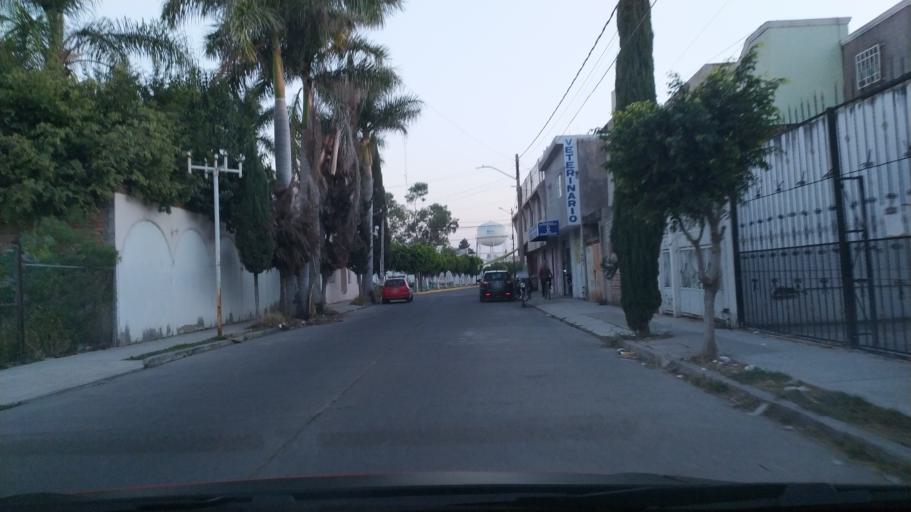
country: MX
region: Guanajuato
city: San Francisco del Rincon
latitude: 21.0105
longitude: -101.8606
